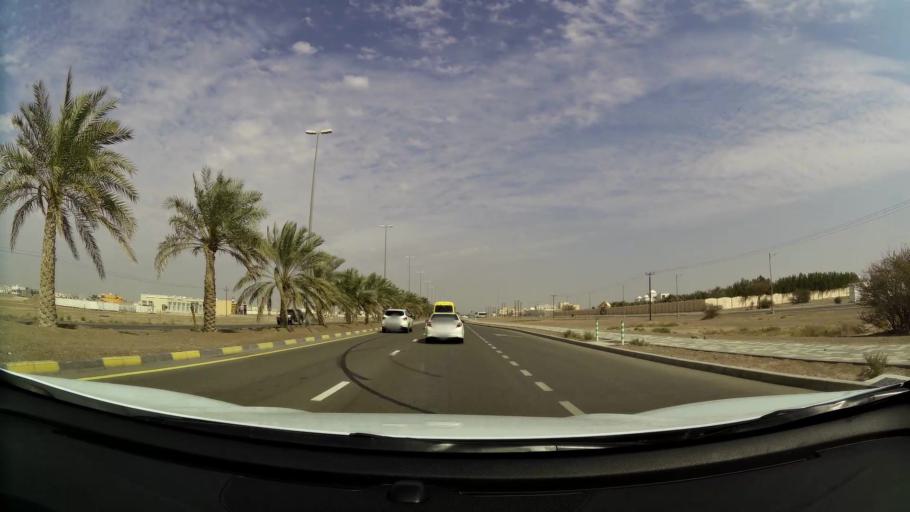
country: AE
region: Abu Dhabi
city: Al Ain
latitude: 24.0878
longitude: 55.8427
